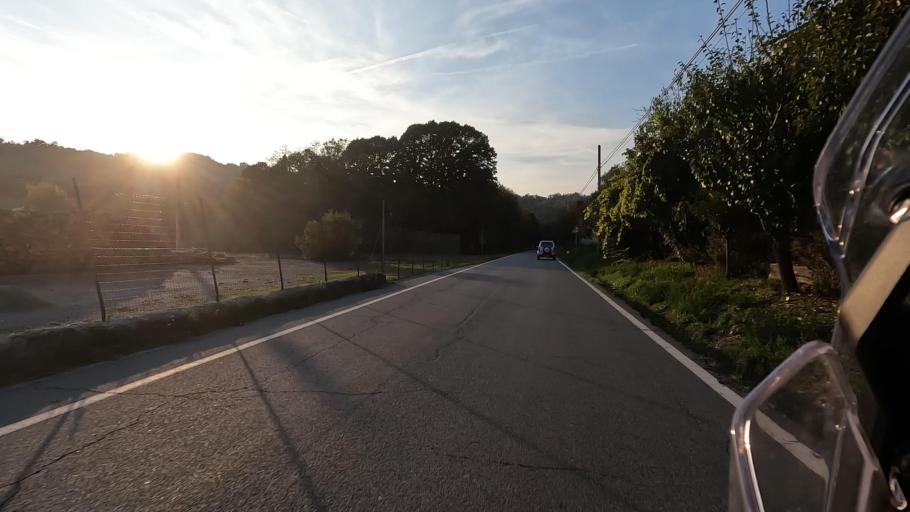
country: IT
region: Liguria
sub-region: Provincia di Savona
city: Sassello
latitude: 44.5007
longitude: 8.4872
